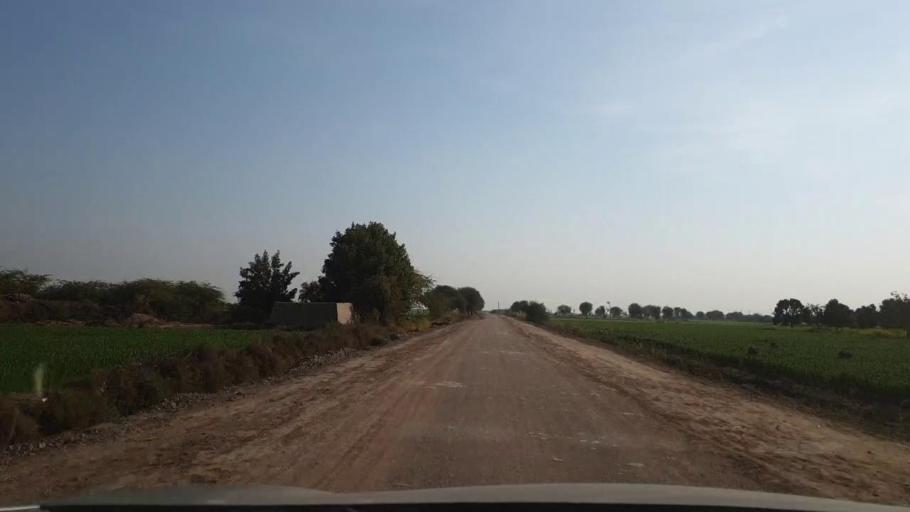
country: PK
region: Sindh
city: Berani
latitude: 25.7204
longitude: 68.8066
